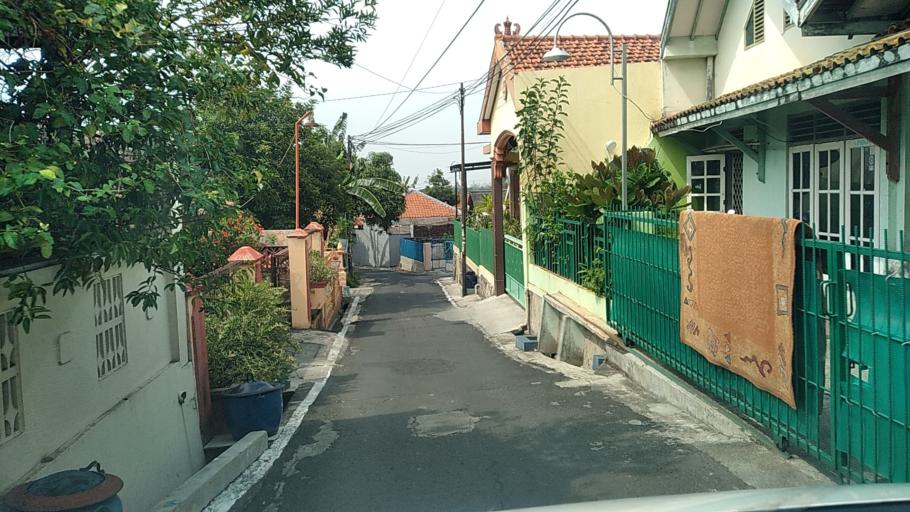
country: ID
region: Central Java
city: Semarang
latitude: -7.0360
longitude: 110.4227
